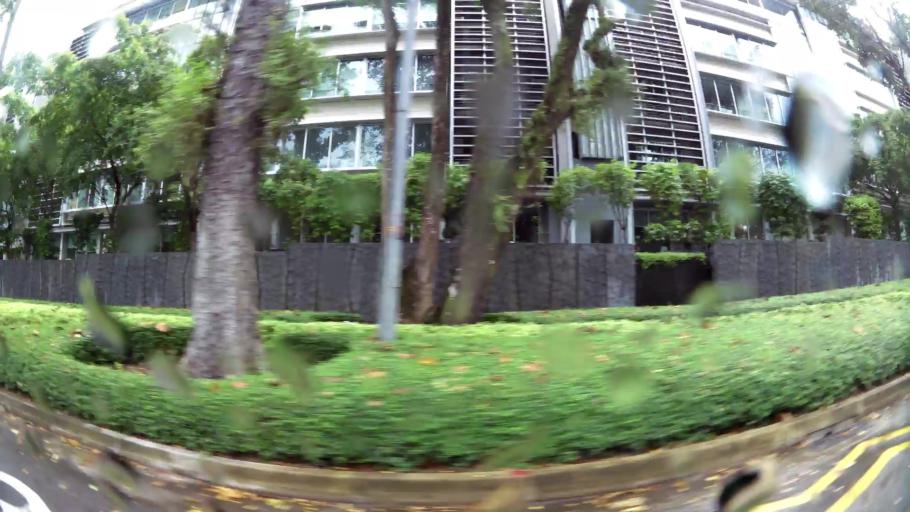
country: SG
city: Singapore
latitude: 1.3084
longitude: 103.8236
